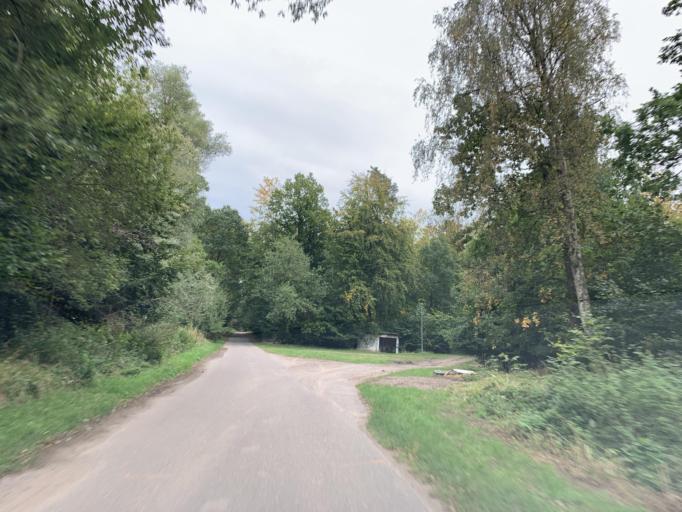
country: DE
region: Mecklenburg-Vorpommern
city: Woldegk
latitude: 53.3273
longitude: 13.5991
